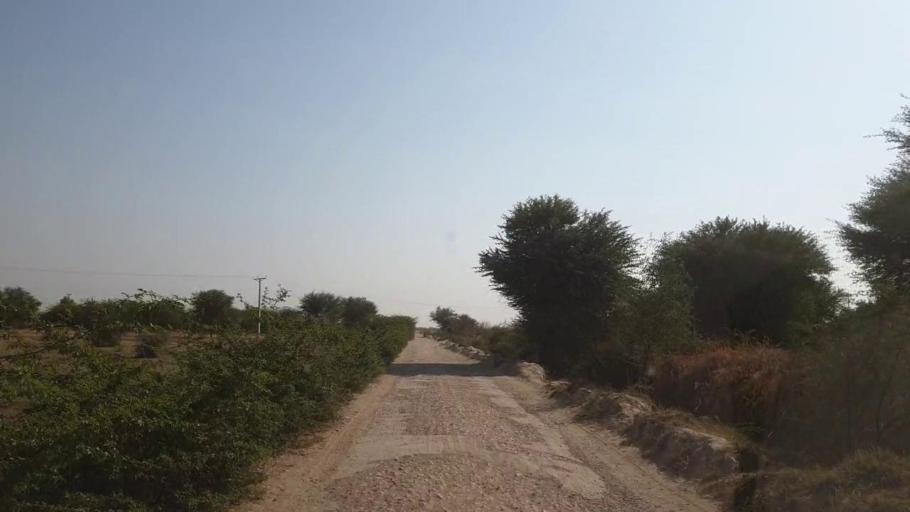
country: PK
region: Sindh
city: Nabisar
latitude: 25.0260
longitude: 69.4946
